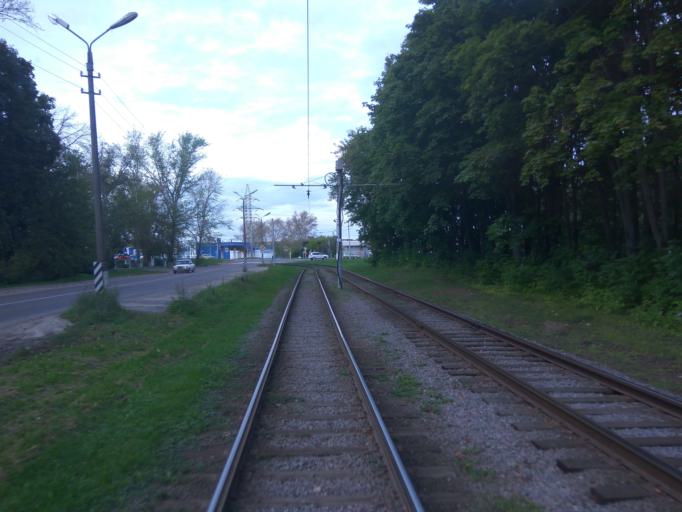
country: RU
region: Moskovskaya
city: Kolomna
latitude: 55.0791
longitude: 38.8168
